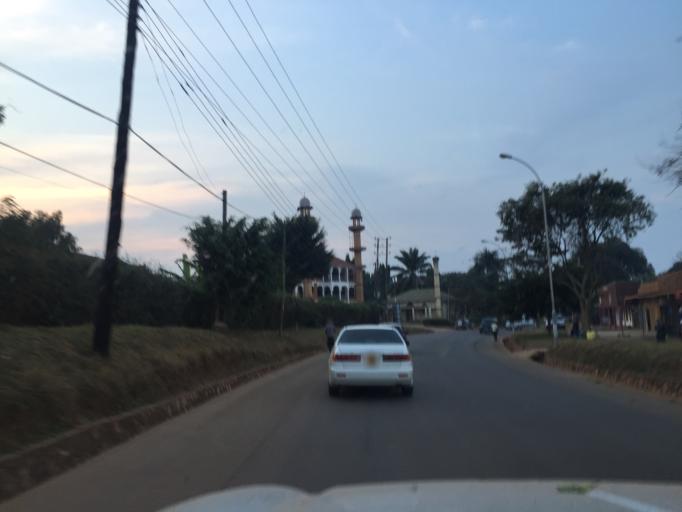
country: UG
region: Central Region
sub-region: Kampala District
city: Kampala
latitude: 0.2491
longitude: 32.6259
